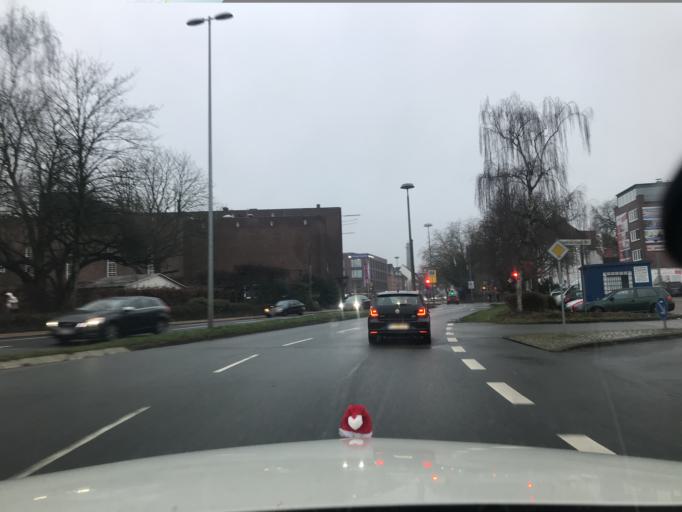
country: DE
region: Schleswig-Holstein
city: Flensburg
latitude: 54.7818
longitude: 9.4391
